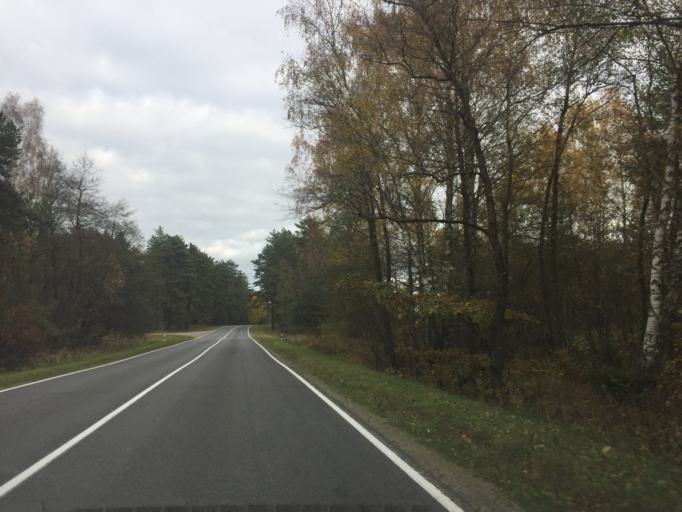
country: BY
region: Minsk
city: Svir
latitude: 54.8822
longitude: 26.3713
